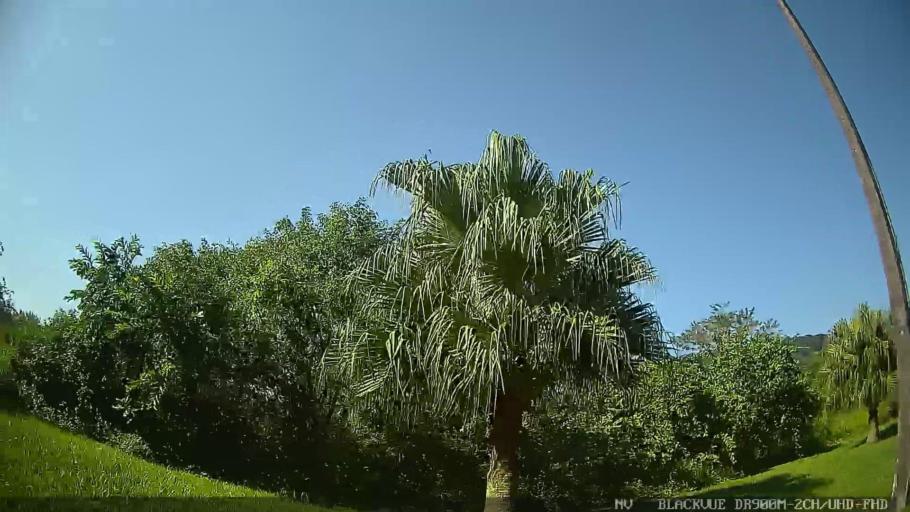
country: BR
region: Sao Paulo
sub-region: Guaruja
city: Guaruja
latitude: -24.0037
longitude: -46.2885
